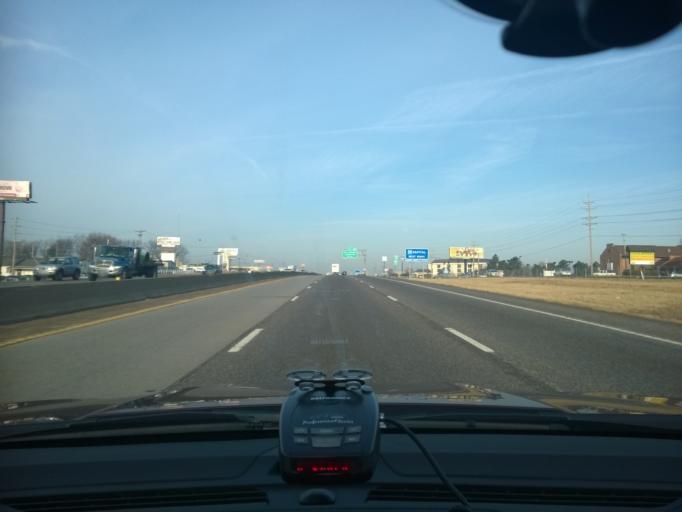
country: US
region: Missouri
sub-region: Saint Charles County
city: Saint Peters
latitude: 38.7907
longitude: -90.5548
